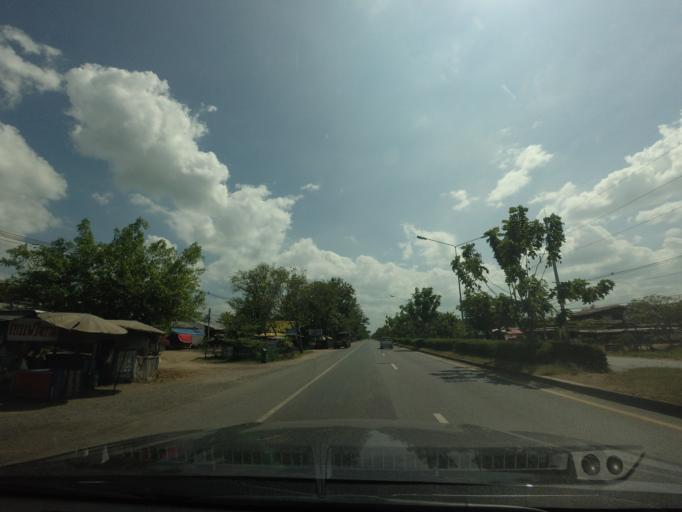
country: TH
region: Phetchabun
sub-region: Amphoe Bueng Sam Phan
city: Bueng Sam Phan
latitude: 15.8595
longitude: 101.0119
